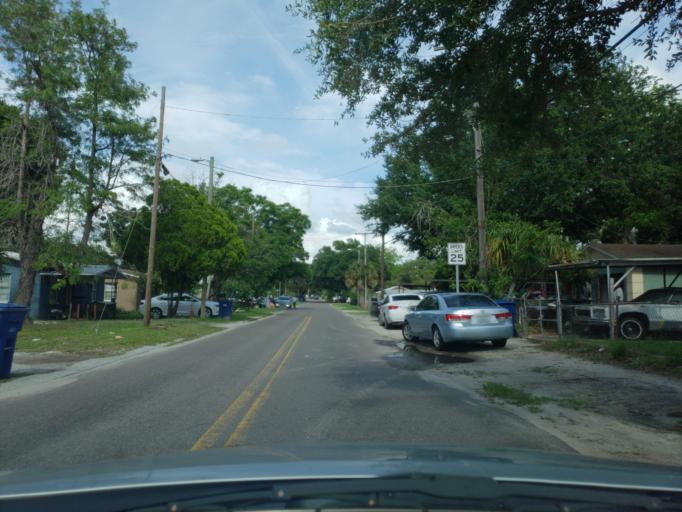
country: US
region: Florida
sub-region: Hillsborough County
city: East Lake-Orient Park
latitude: 27.9851
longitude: -82.4263
